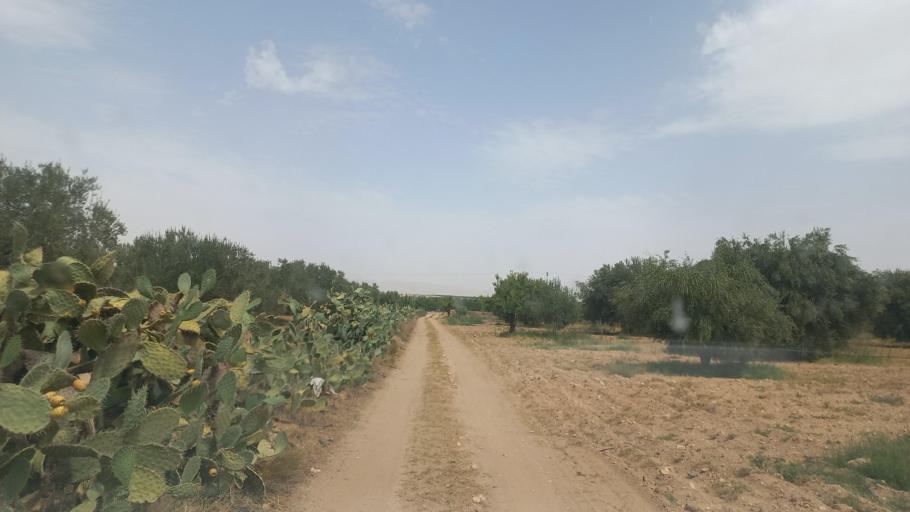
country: TN
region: Al Qasrayn
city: Kasserine
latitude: 35.2635
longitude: 9.0005
